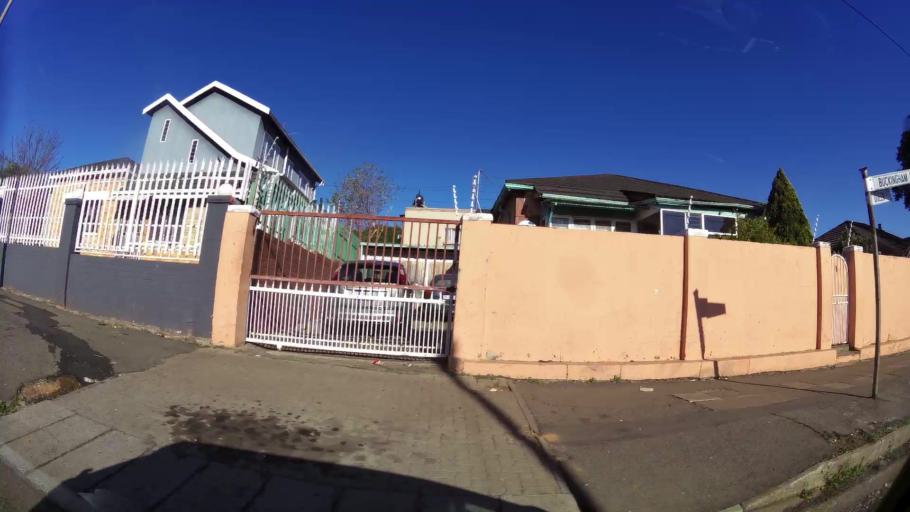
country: ZA
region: Gauteng
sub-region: City of Johannesburg Metropolitan Municipality
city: Johannesburg
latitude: -26.1971
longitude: 28.1126
